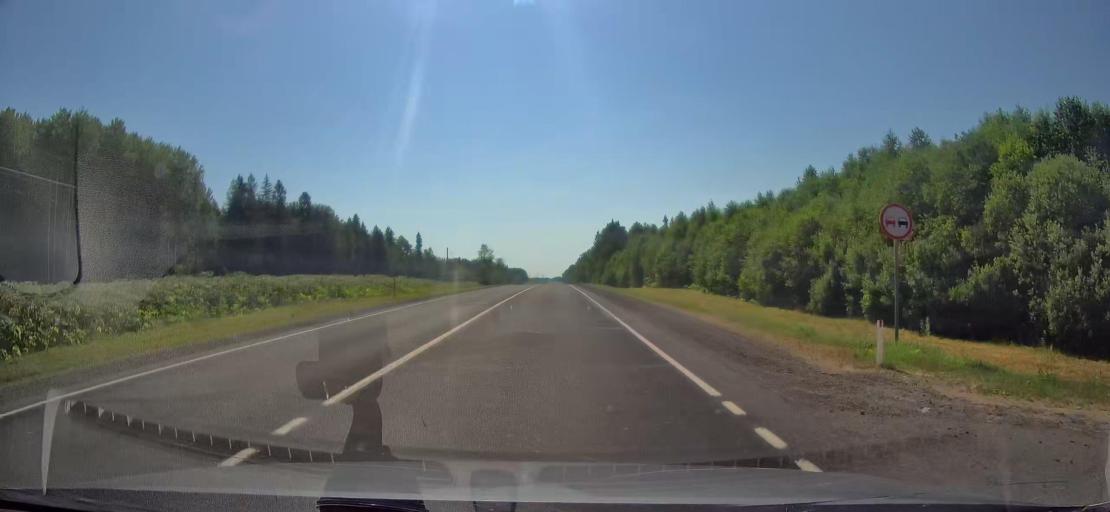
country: RU
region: Vologda
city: Sazonovo
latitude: 59.0764
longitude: 35.2954
